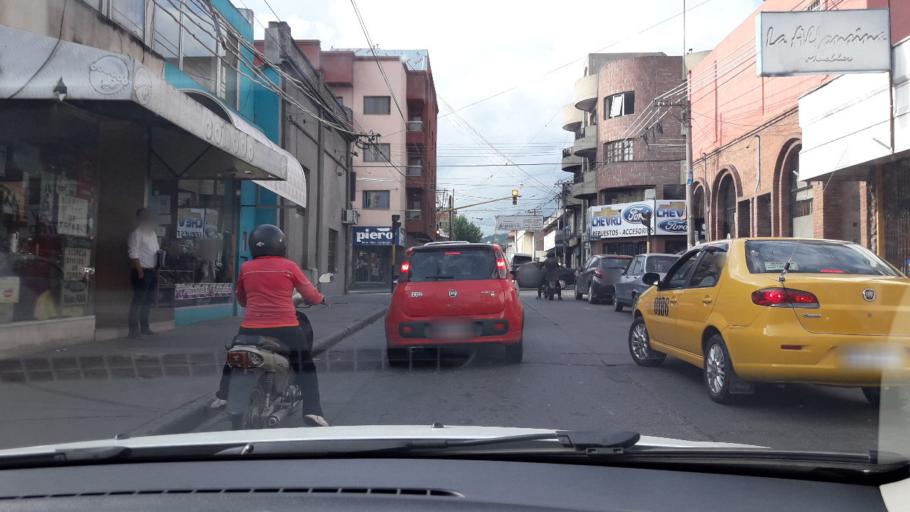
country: AR
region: Jujuy
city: San Salvador de Jujuy
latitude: -24.1911
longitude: -65.2988
